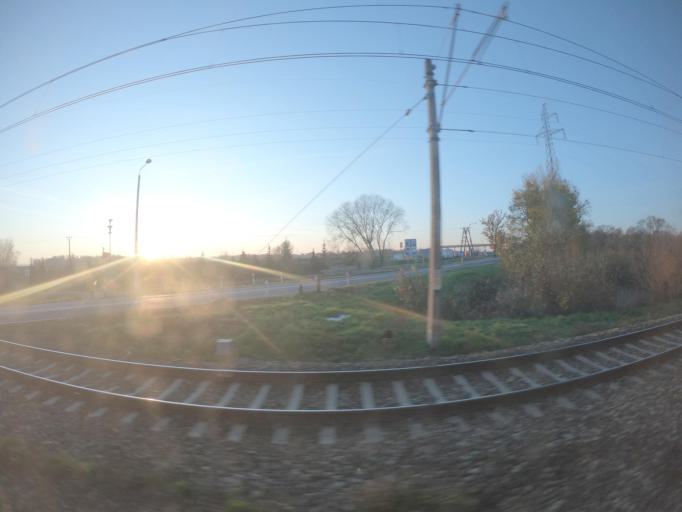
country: PL
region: Lubusz
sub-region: Powiat gorzowski
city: Kostrzyn nad Odra
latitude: 52.5748
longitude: 14.6438
